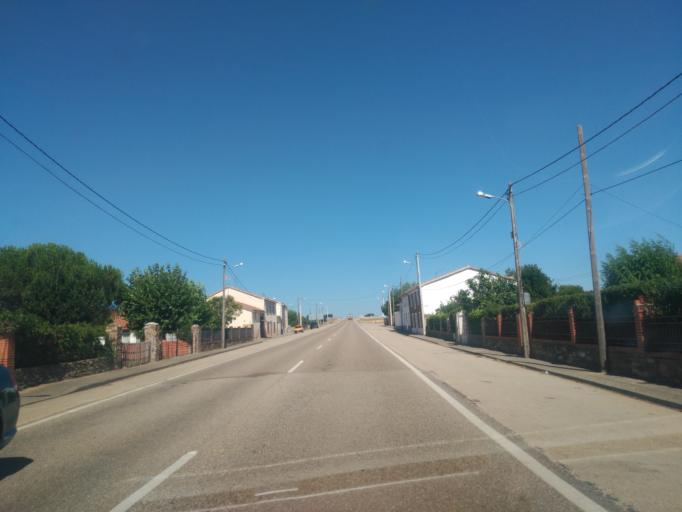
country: ES
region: Castille and Leon
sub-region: Provincia de Zamora
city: Pozuelo de Tabara
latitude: 41.7863
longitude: -5.8972
